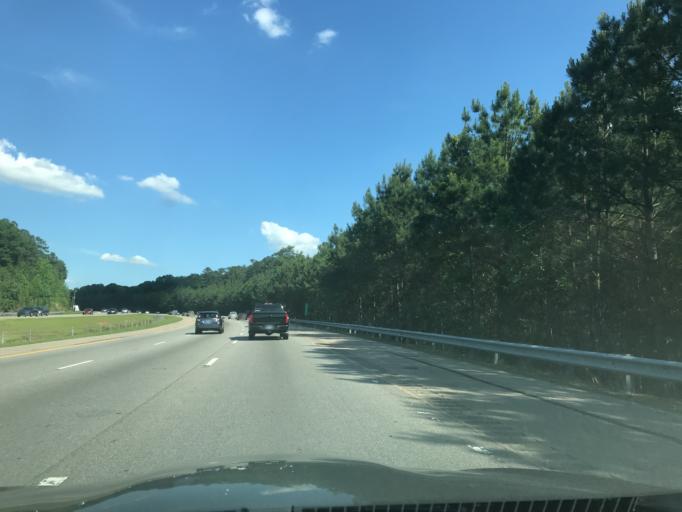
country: US
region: North Carolina
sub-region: Wake County
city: West Raleigh
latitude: 35.9013
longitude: -78.6309
